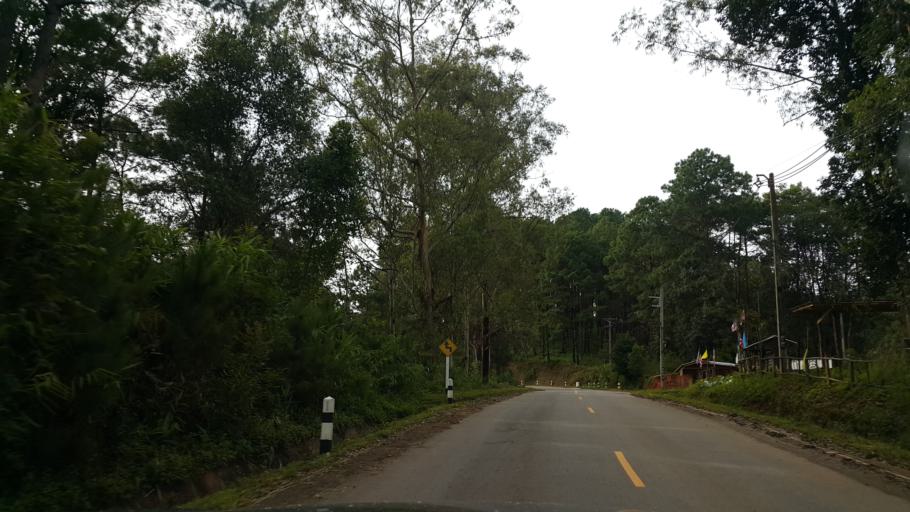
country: TH
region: Chiang Mai
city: Chaem Luang
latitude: 18.9452
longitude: 98.4549
